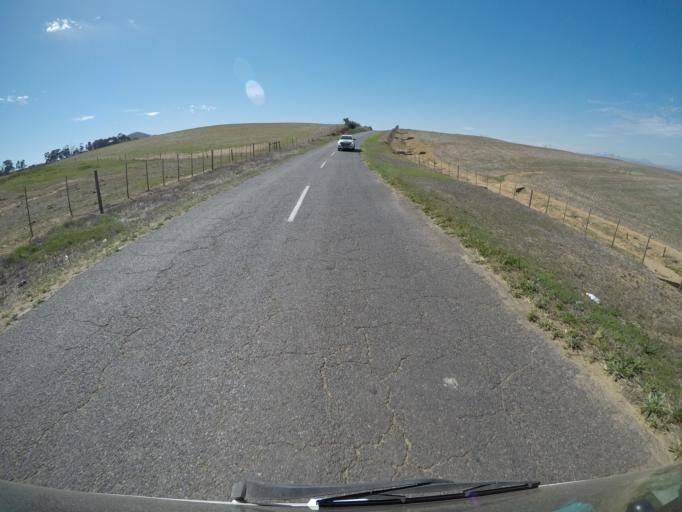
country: ZA
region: Western Cape
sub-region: City of Cape Town
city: Sunset Beach
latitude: -33.7429
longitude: 18.5612
